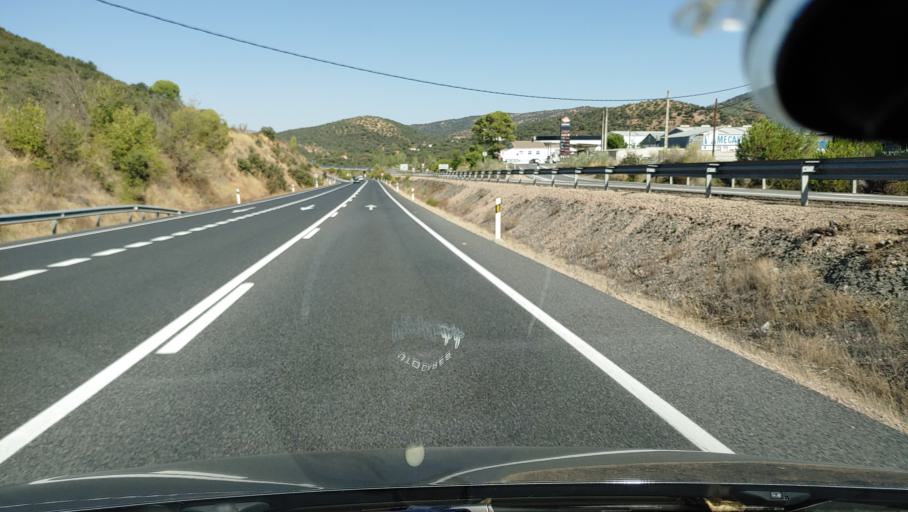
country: ES
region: Andalusia
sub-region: Province of Cordoba
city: Villaharta
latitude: 38.1232
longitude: -4.8981
